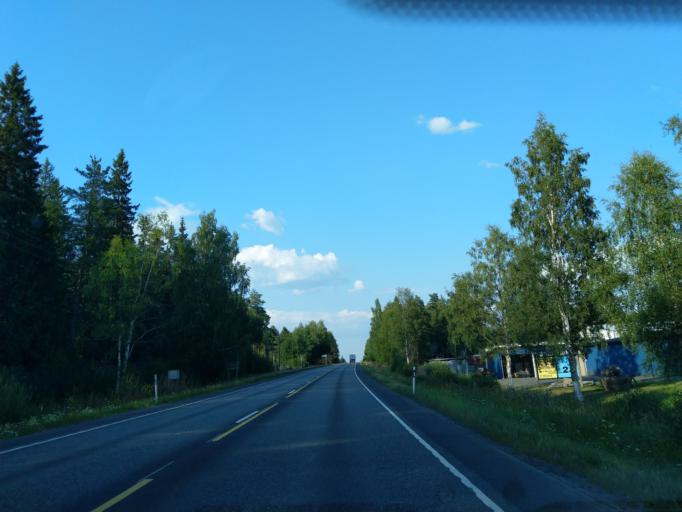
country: FI
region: Satakunta
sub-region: Pori
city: Pomarkku
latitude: 61.7023
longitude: 22.0156
